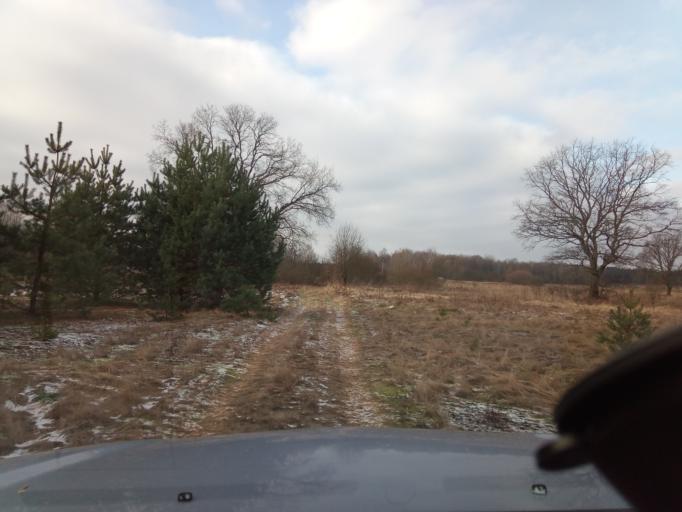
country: LT
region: Alytaus apskritis
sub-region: Alytaus rajonas
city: Daugai
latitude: 54.1158
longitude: 24.2347
